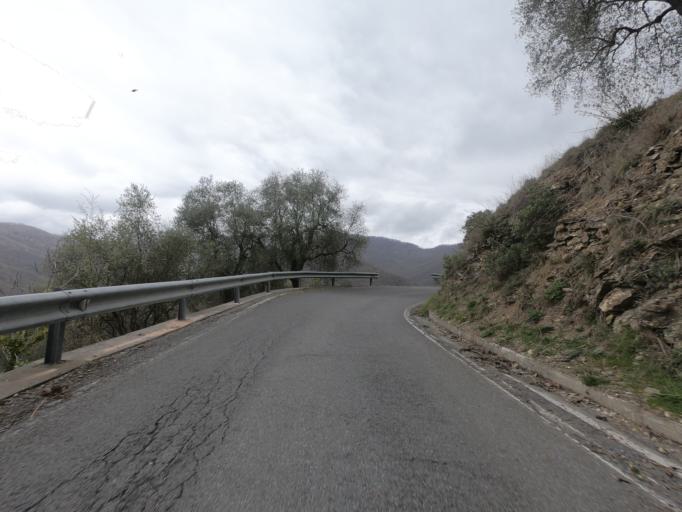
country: IT
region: Liguria
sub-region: Provincia di Savona
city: Testico
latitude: 44.0269
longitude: 8.0107
